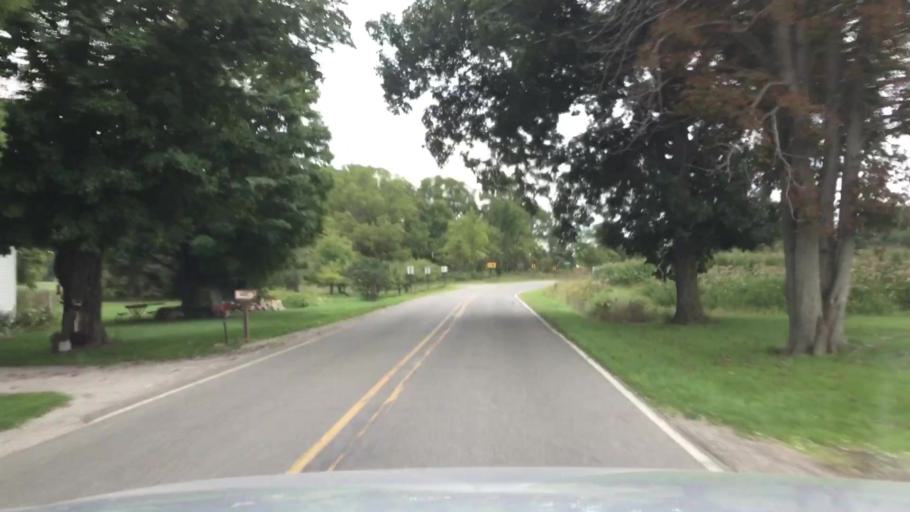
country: US
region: Michigan
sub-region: Shiawassee County
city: Durand
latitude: 42.8446
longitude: -84.0344
